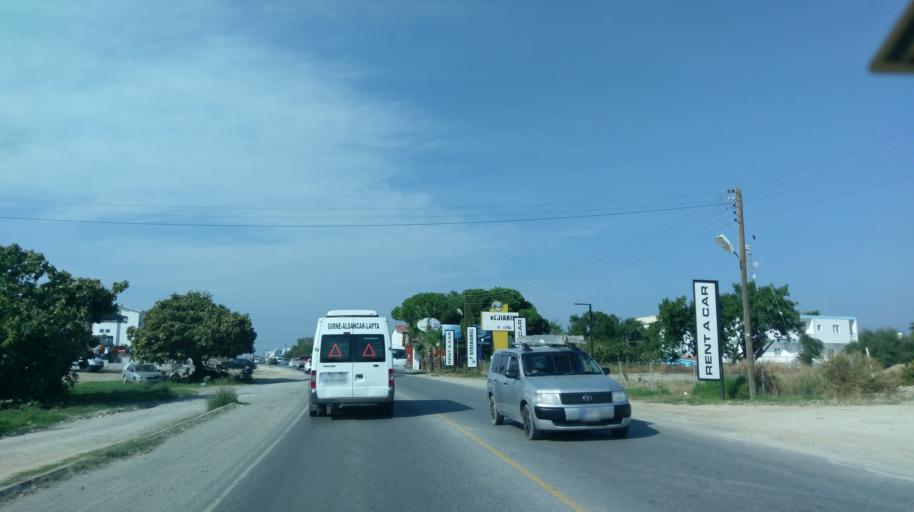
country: CY
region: Keryneia
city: Lapithos
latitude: 35.3477
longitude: 33.2258
